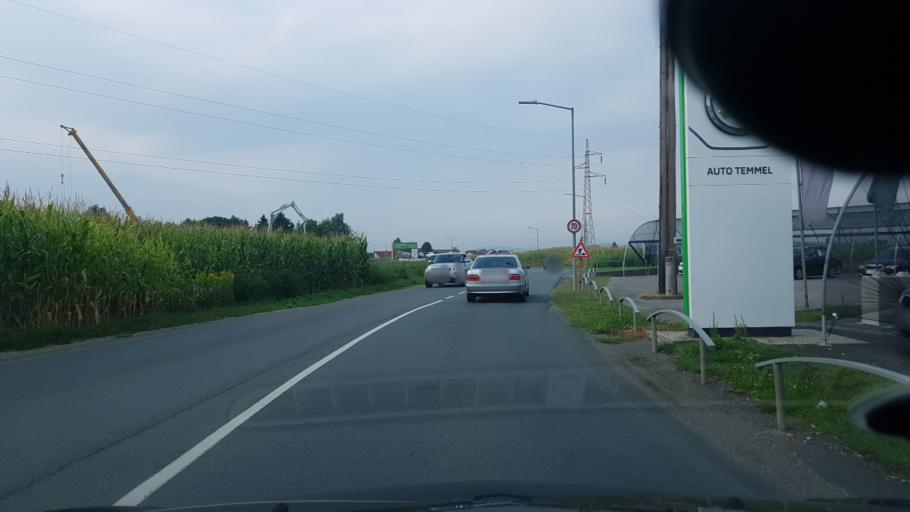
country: AT
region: Styria
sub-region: Politischer Bezirk Leibnitz
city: Kaindorf an der Sulm
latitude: 46.8040
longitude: 15.5634
